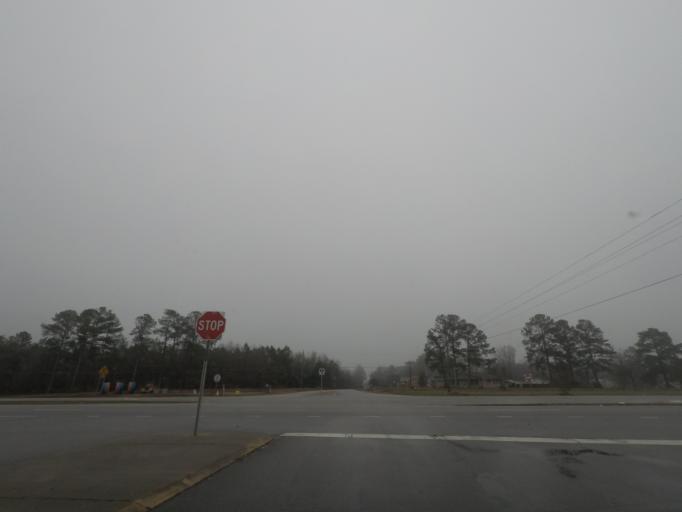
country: US
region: North Carolina
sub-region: Scotland County
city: Laurinburg
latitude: 34.8040
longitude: -79.4384
